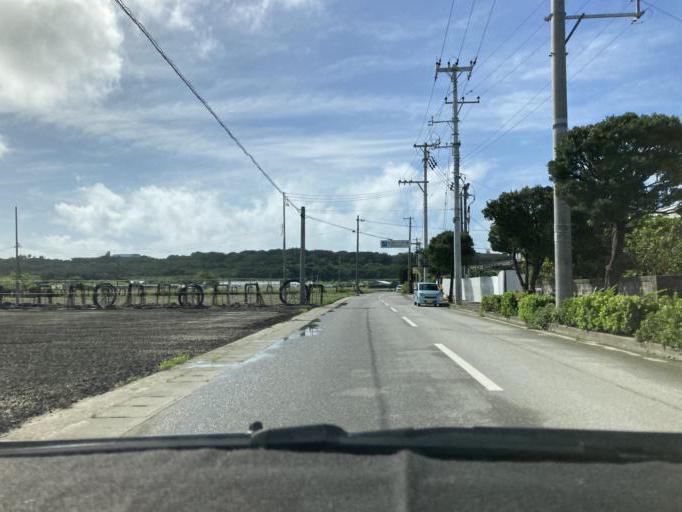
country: JP
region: Okinawa
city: Itoman
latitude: 26.1008
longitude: 127.6616
